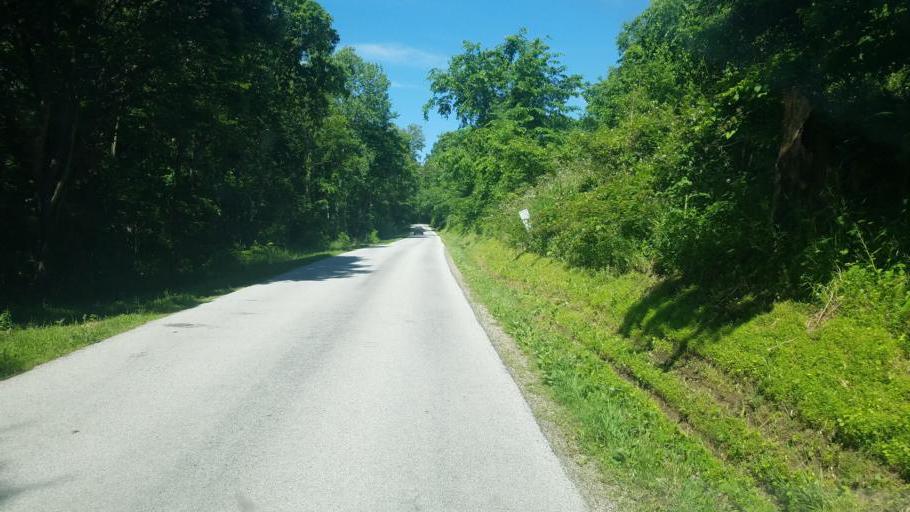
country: US
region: Ohio
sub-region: Coshocton County
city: Coshocton
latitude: 40.2288
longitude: -81.8211
